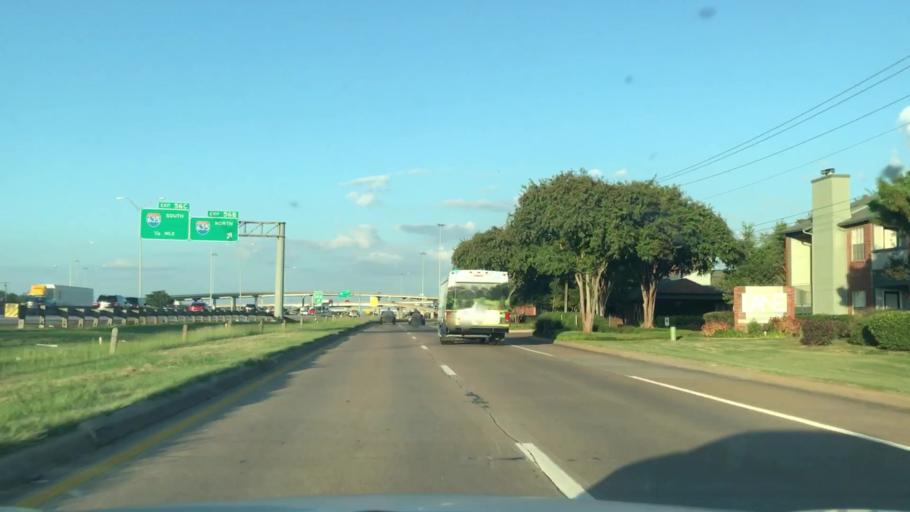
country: US
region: Texas
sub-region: Dallas County
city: Mesquite
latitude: 32.8194
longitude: -96.6354
